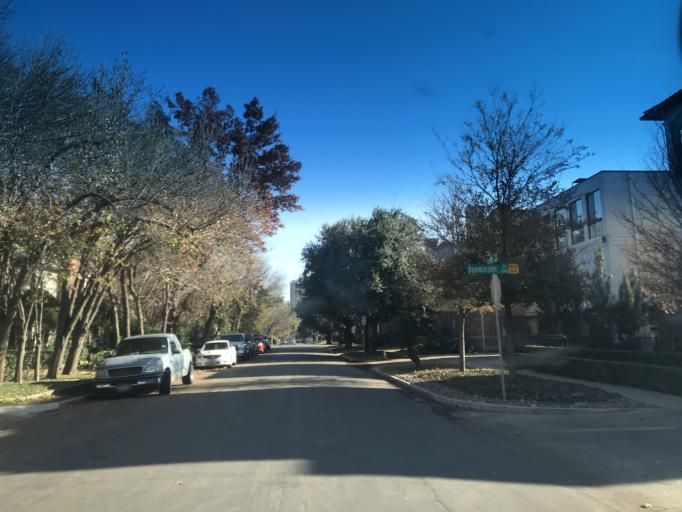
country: US
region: Texas
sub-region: Dallas County
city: Highland Park
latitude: 32.8152
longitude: -96.8076
